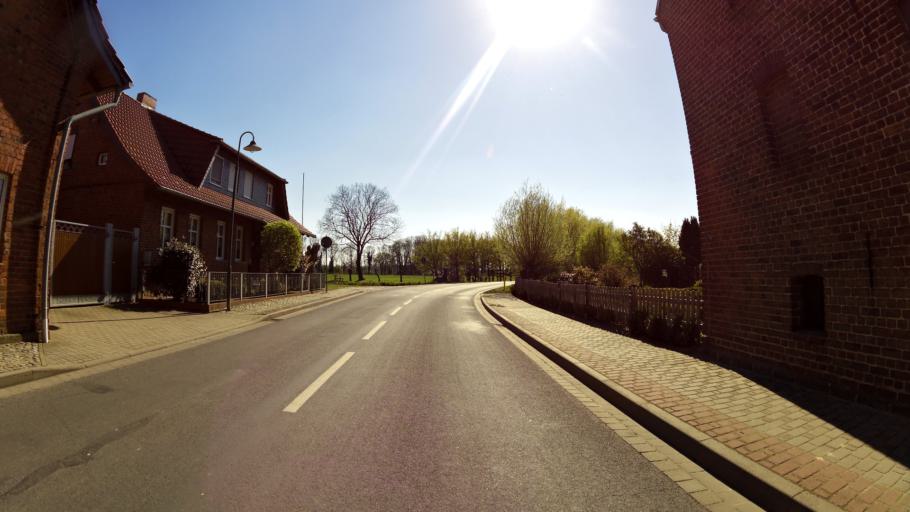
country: DE
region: Saxony-Anhalt
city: Uchtspringe
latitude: 52.6279
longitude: 11.6542
